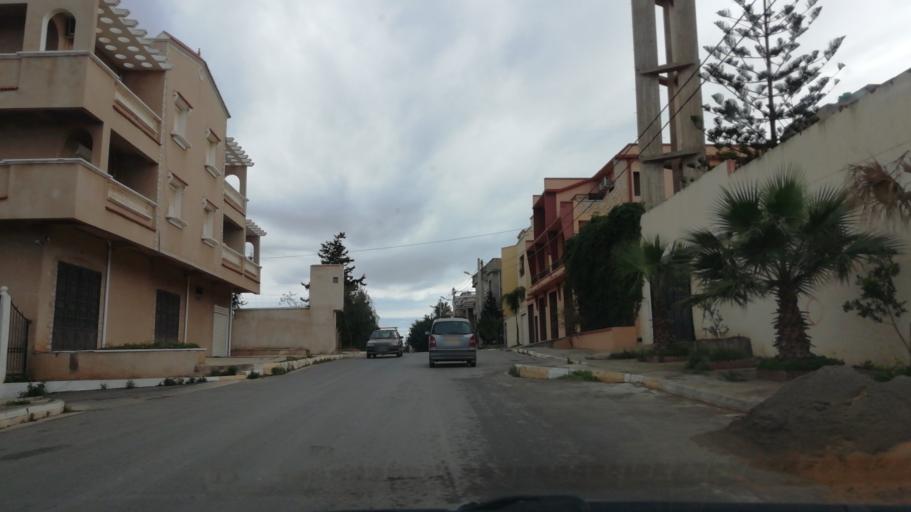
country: DZ
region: Oran
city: Oran
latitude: 35.6952
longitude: -0.6008
